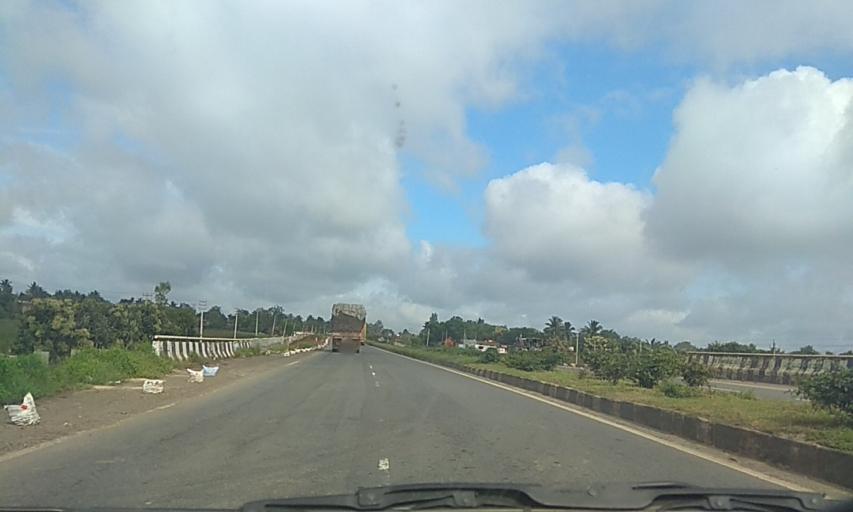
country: IN
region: Karnataka
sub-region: Haveri
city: Shiggaon
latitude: 15.0112
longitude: 75.1952
